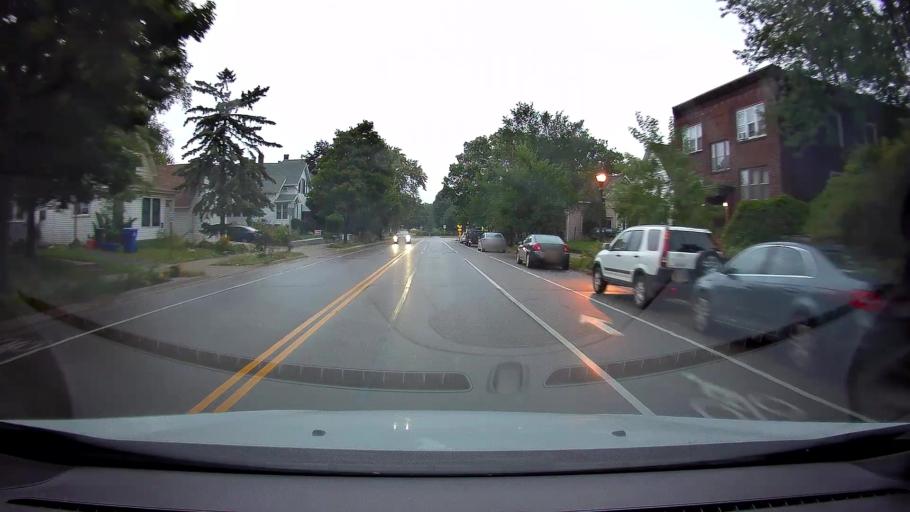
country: US
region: Minnesota
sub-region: Ramsey County
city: Lauderdale
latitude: 44.9672
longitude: -93.1979
